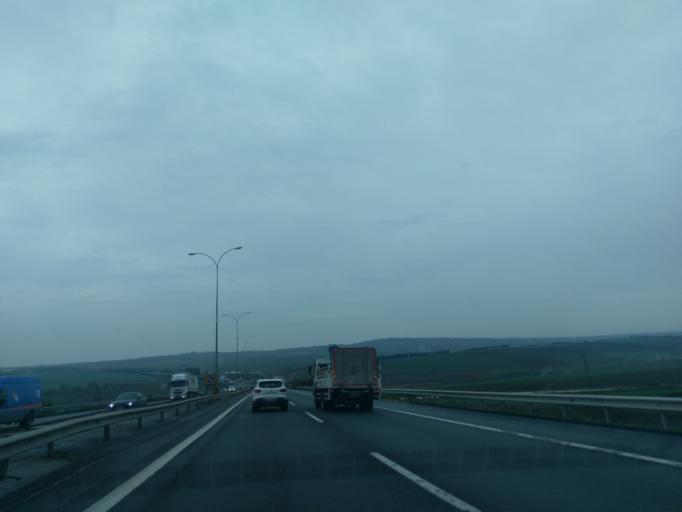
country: TR
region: Istanbul
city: Silivri
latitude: 41.1167
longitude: 28.2558
